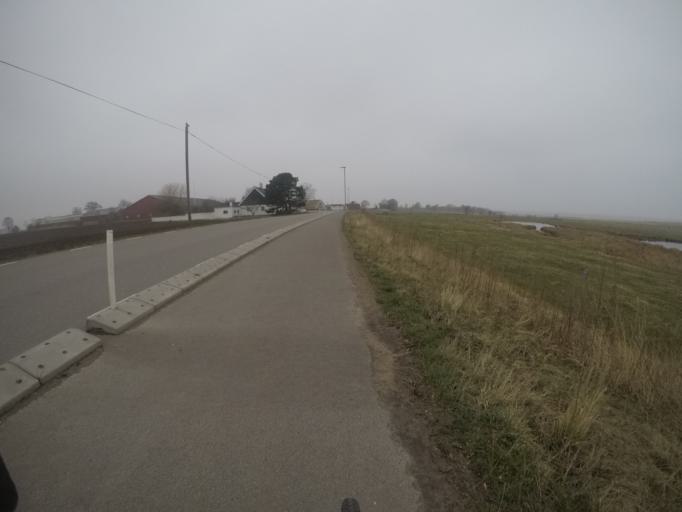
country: SE
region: Skane
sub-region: Angelholms Kommun
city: Vejbystrand
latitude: 56.2225
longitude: 12.7475
